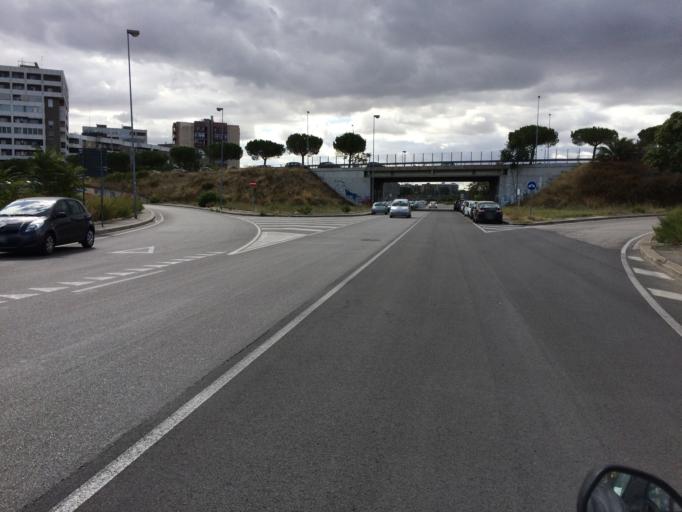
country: IT
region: Apulia
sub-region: Provincia di Bari
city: Bari
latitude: 41.0943
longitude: 16.8576
